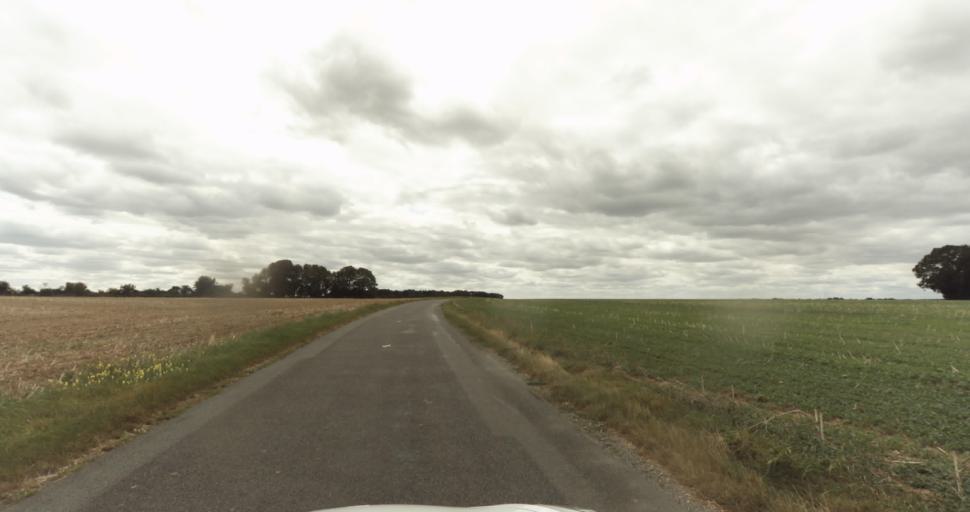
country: FR
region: Haute-Normandie
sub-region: Departement de l'Eure
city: Saint-Germain-sur-Avre
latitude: 48.8154
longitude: 1.2664
